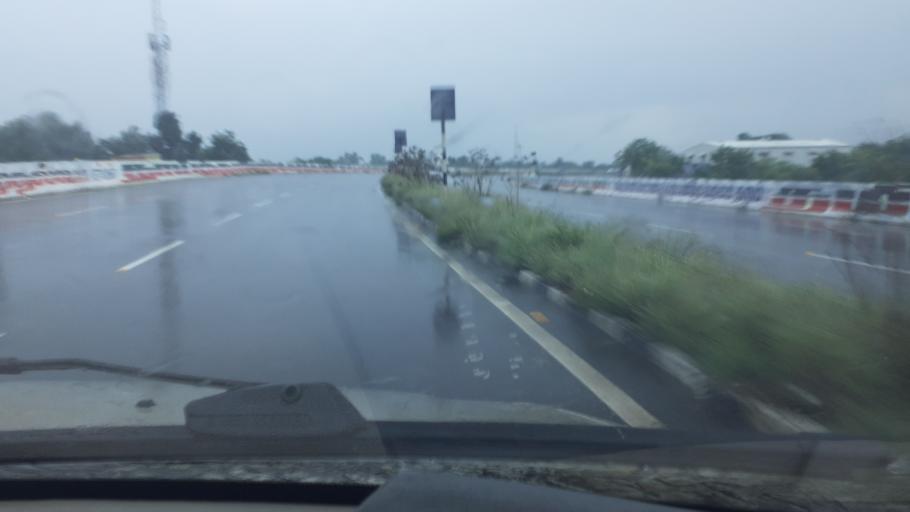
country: IN
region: Tamil Nadu
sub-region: Virudhunagar
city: Virudunagar
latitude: 9.6021
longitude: 77.9547
